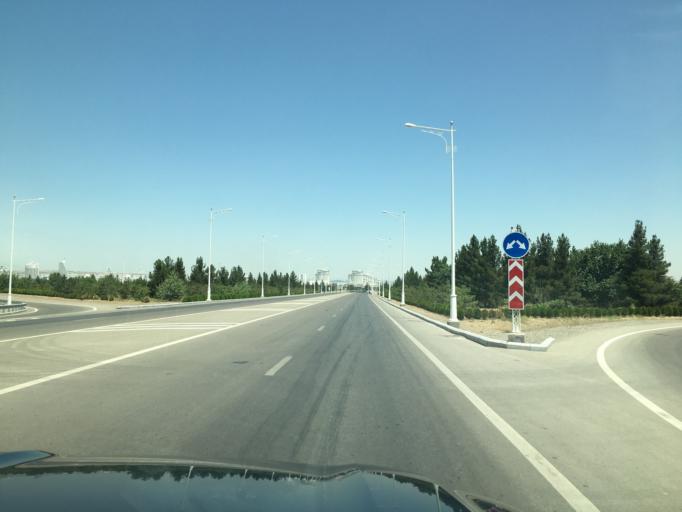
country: TM
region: Ahal
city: Ashgabat
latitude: 37.8610
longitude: 58.3763
